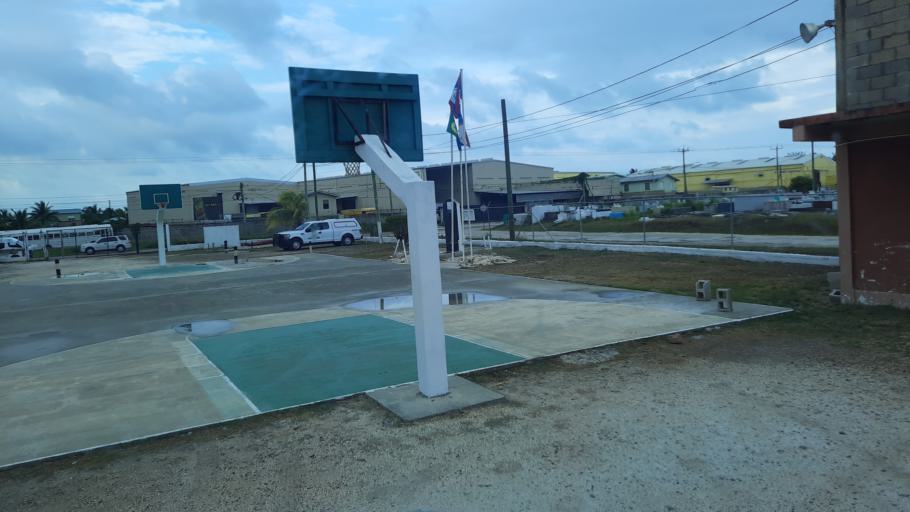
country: BZ
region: Belize
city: Belize City
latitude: 17.4986
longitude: -88.2080
